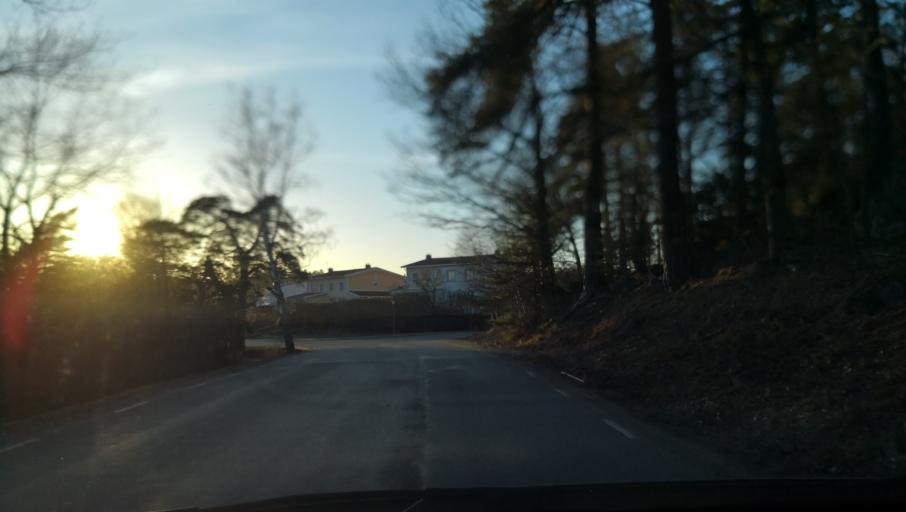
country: SE
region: Stockholm
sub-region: Varmdo Kommun
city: Gustavsberg
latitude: 59.3302
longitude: 18.4090
